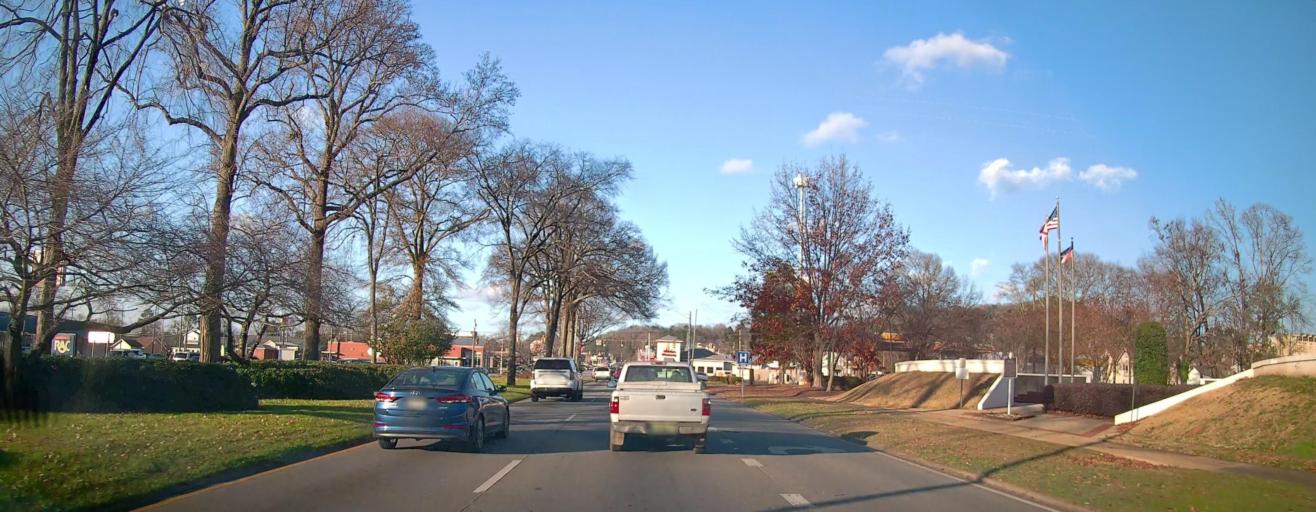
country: US
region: Alabama
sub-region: Calhoun County
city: Anniston
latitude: 33.6665
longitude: -85.8266
